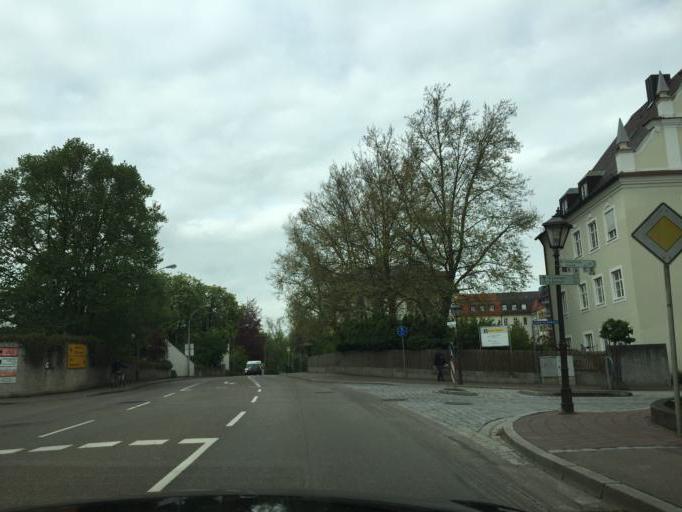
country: DE
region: Bavaria
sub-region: Swabia
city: Dillingen an der Donau
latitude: 48.5767
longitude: 10.4895
